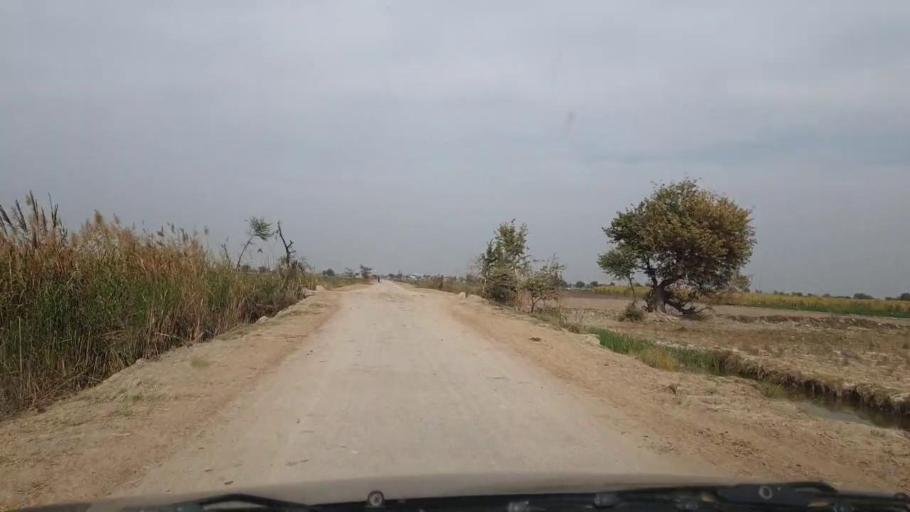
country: PK
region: Sindh
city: Sinjhoro
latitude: 26.0940
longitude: 68.8277
